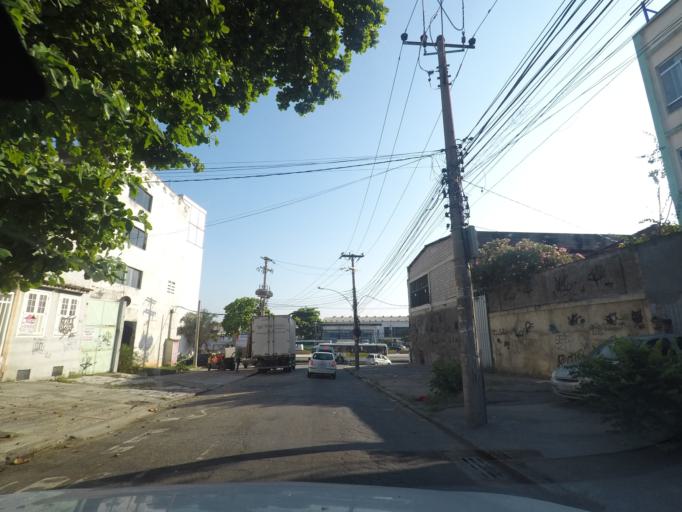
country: BR
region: Rio de Janeiro
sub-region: Rio De Janeiro
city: Rio de Janeiro
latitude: -22.8451
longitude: -43.2501
